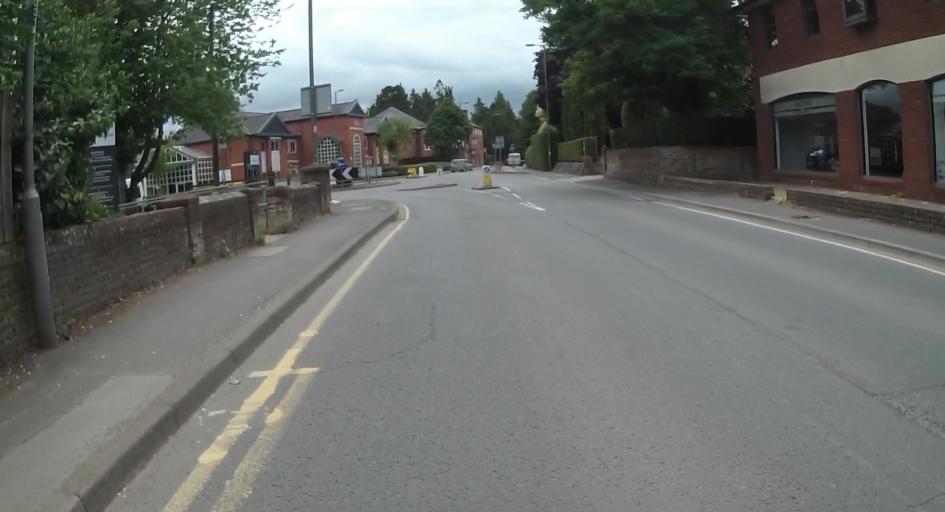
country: GB
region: England
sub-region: Surrey
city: Farnham
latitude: 51.2118
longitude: -0.8082
